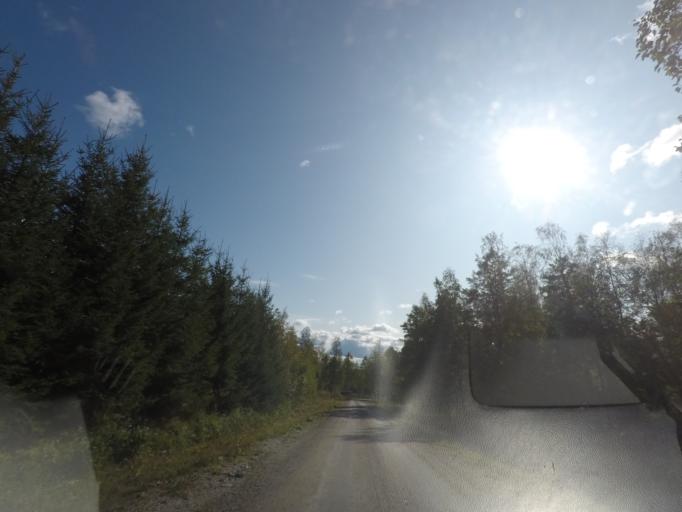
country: SE
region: Vaestmanland
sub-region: Skinnskattebergs Kommun
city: Skinnskatteberg
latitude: 59.8283
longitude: 15.5216
